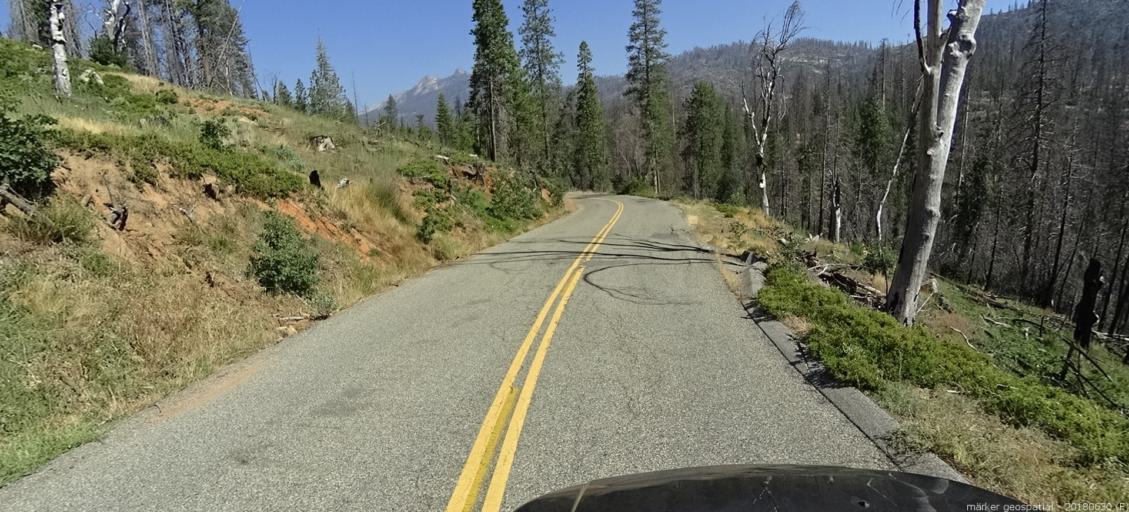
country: US
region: California
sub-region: Fresno County
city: Auberry
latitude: 37.2870
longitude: -119.3578
